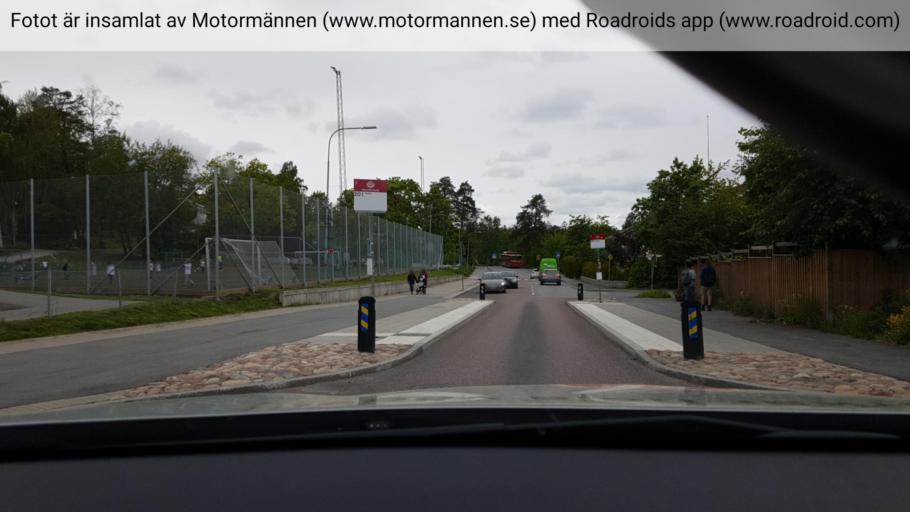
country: SE
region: Stockholm
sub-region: Lidingo
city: Brevik
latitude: 59.3455
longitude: 18.1771
